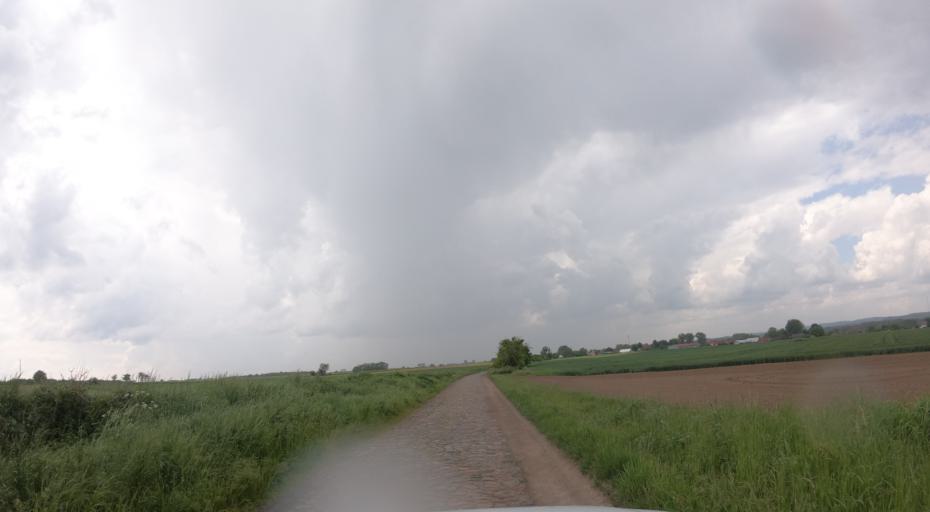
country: PL
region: West Pomeranian Voivodeship
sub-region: Powiat pyrzycki
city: Bielice
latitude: 53.2663
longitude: 14.6919
